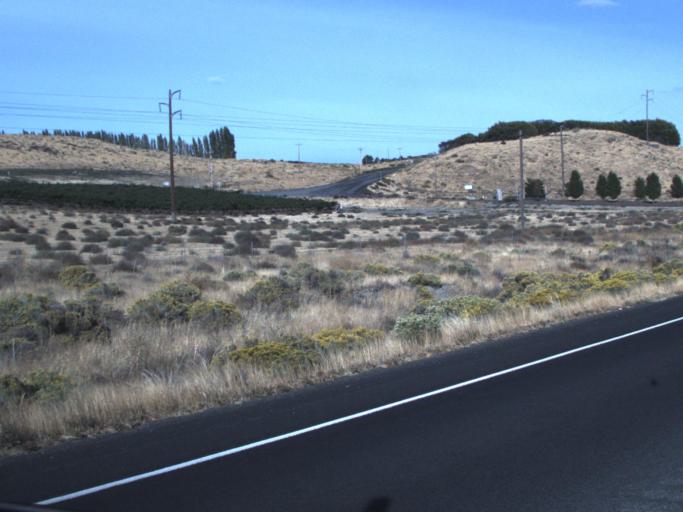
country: US
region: Oregon
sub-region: Morrow County
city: Boardman
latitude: 45.8659
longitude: -119.7821
